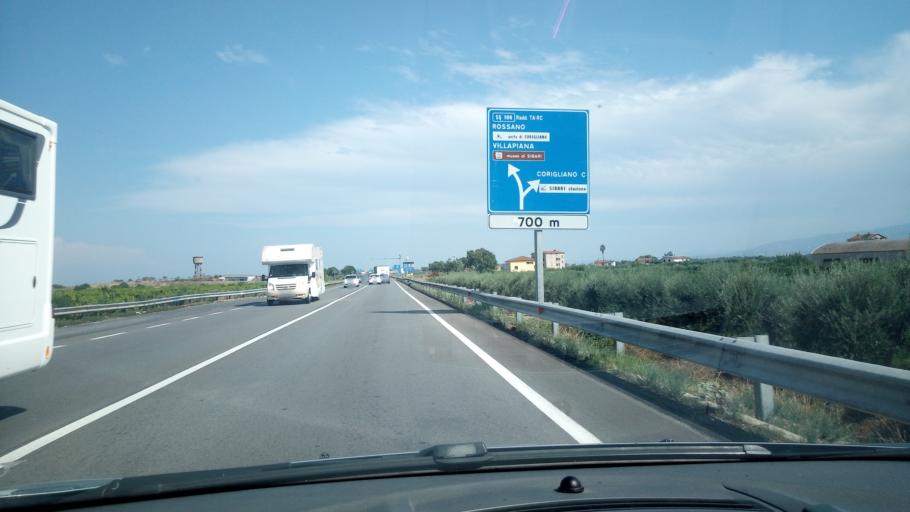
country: IT
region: Calabria
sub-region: Provincia di Cosenza
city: Sibari
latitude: 39.7238
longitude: 16.4380
